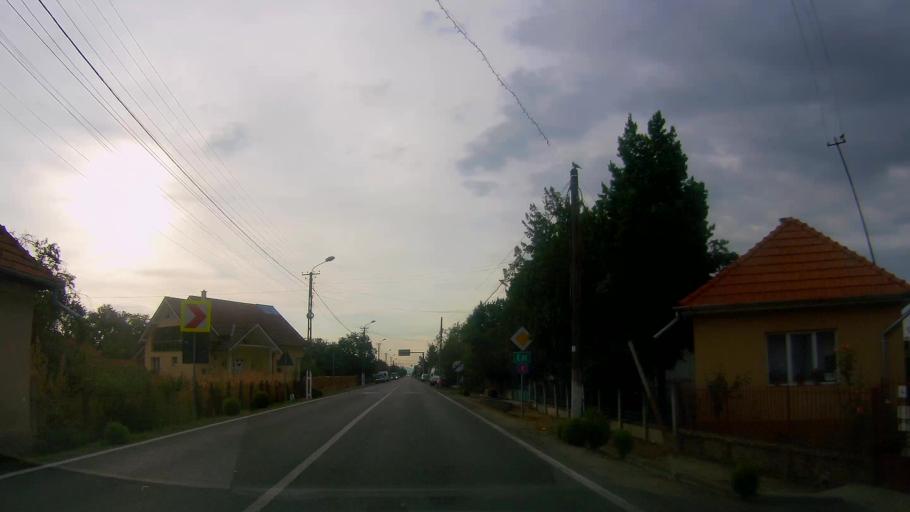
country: RO
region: Satu Mare
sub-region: Comuna Halmeu
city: Halmeu
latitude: 47.9754
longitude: 23.0276
